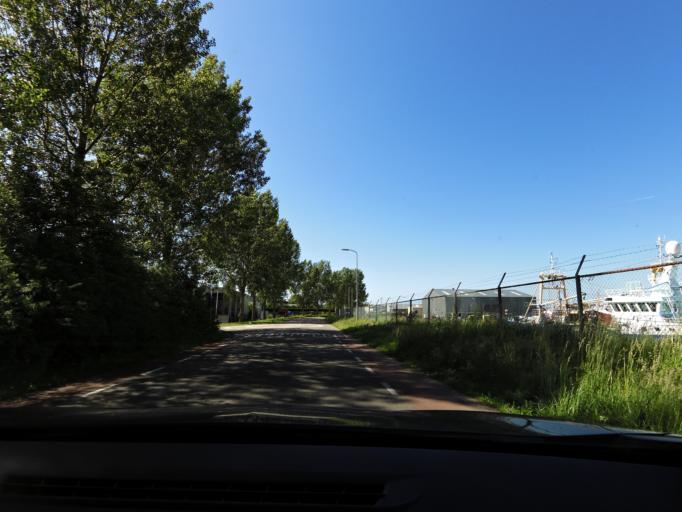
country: NL
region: South Holland
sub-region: Gemeente Goeree-Overflakkee
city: Goedereede
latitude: 51.8171
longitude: 4.0432
